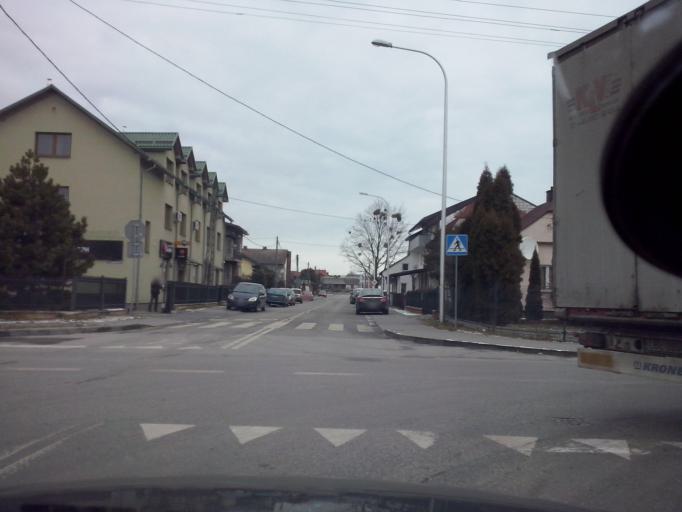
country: PL
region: Lublin Voivodeship
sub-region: Powiat bilgorajski
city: Bilgoraj
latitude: 50.5292
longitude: 22.7232
